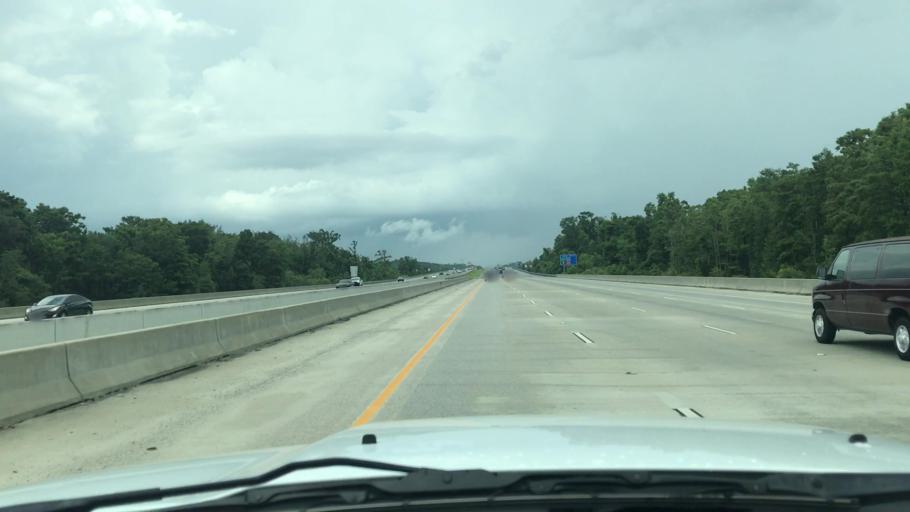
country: US
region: Georgia
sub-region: McIntosh County
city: Darien
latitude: 31.3660
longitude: -81.4570
